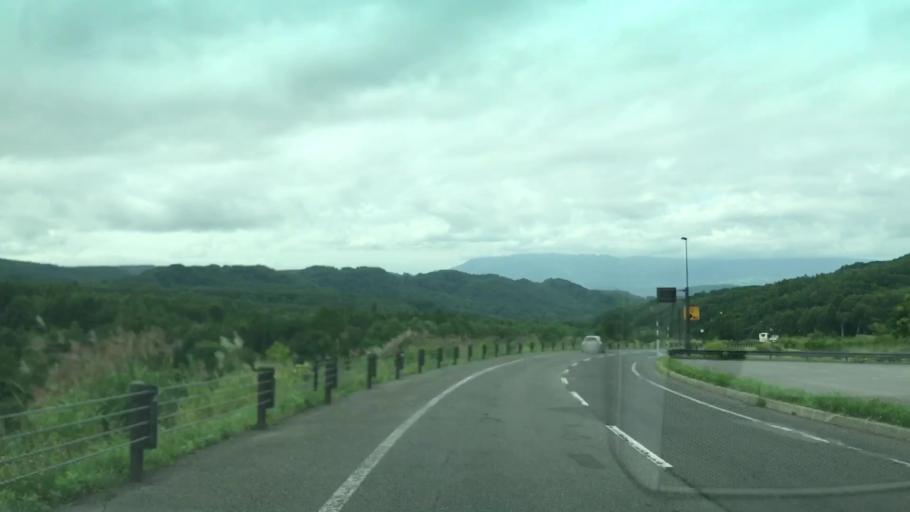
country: JP
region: Hokkaido
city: Niseko Town
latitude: 42.9533
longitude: 140.8618
